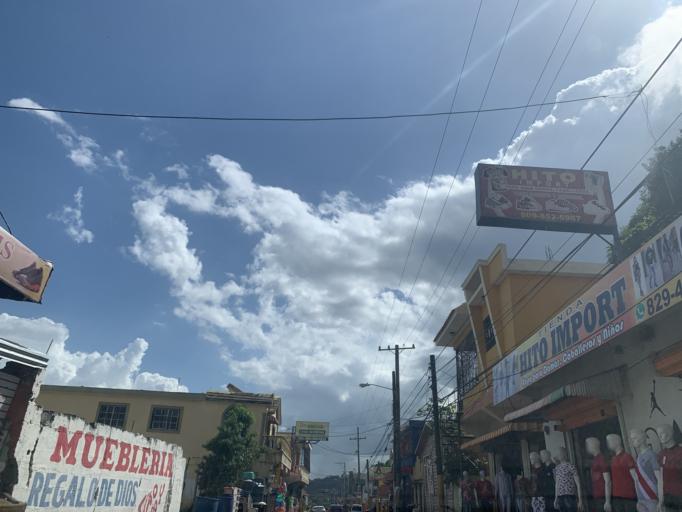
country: DO
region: Monte Plata
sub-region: Yamasa
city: Yamasa
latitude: 18.7717
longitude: -70.0255
